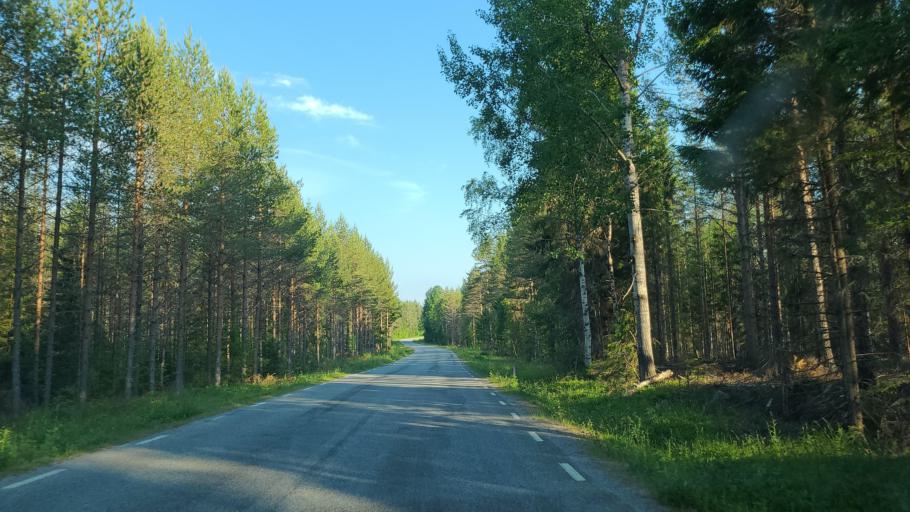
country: SE
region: Vaesterbotten
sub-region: Skelleftea Kommun
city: Burea
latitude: 64.3609
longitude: 21.3343
